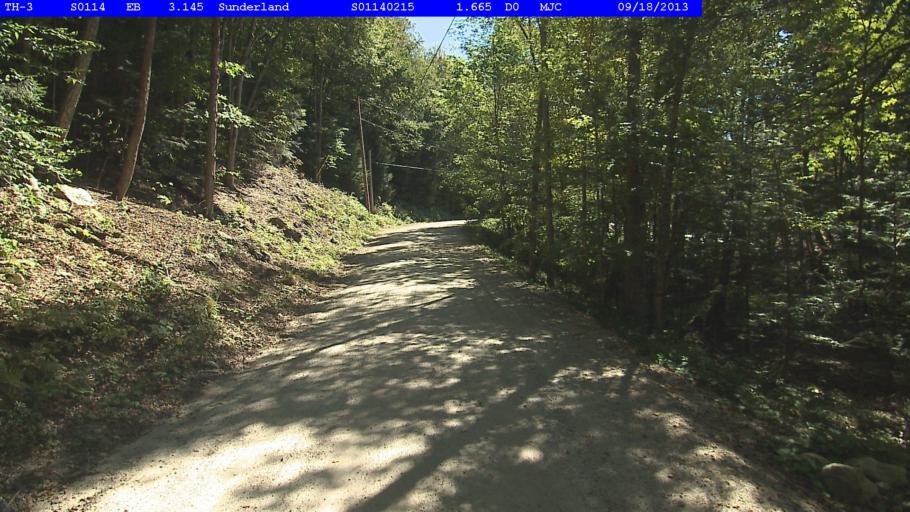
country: US
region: Vermont
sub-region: Bennington County
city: Arlington
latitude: 43.0495
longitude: -73.1159
